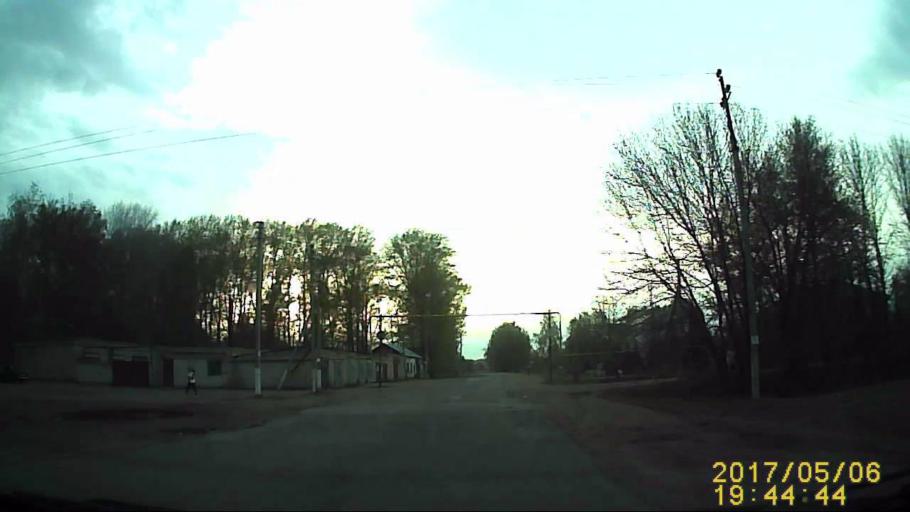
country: RU
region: Ulyanovsk
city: Staraya Mayna
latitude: 54.6073
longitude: 48.9270
